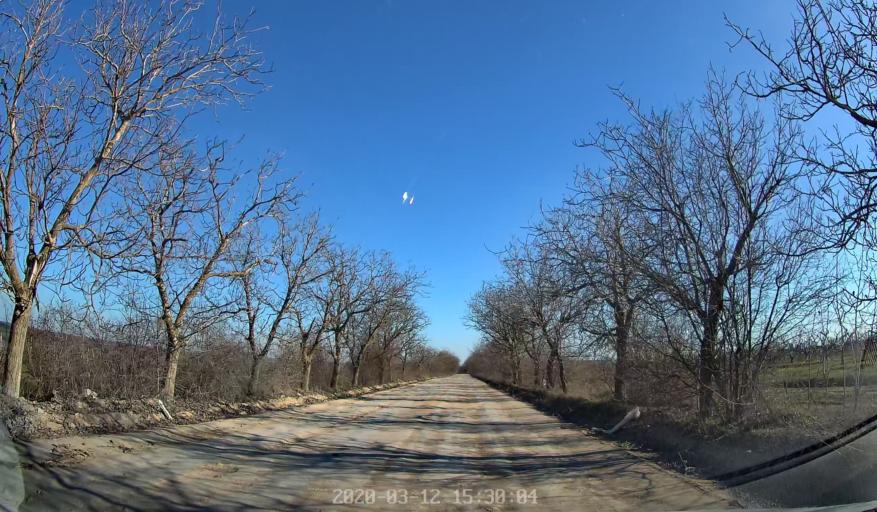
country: MD
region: Chisinau
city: Ciorescu
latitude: 47.1622
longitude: 28.9375
